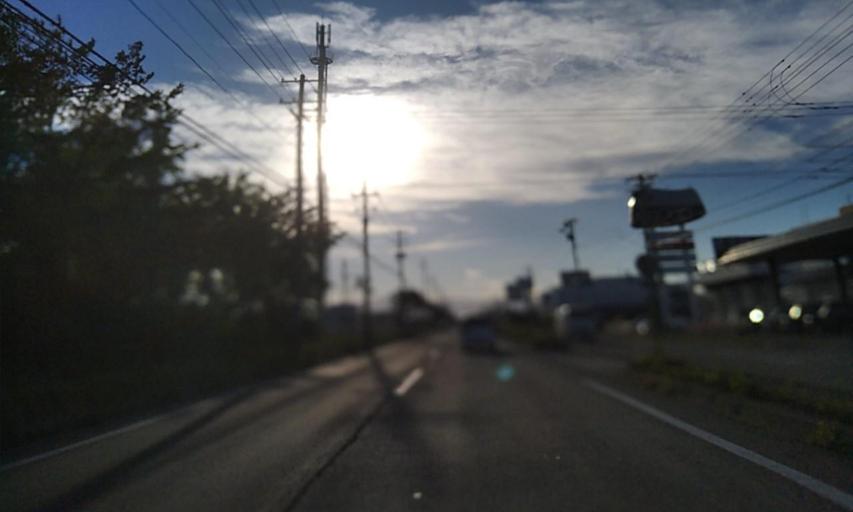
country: JP
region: Hokkaido
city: Obihiro
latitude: 42.9289
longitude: 143.1617
